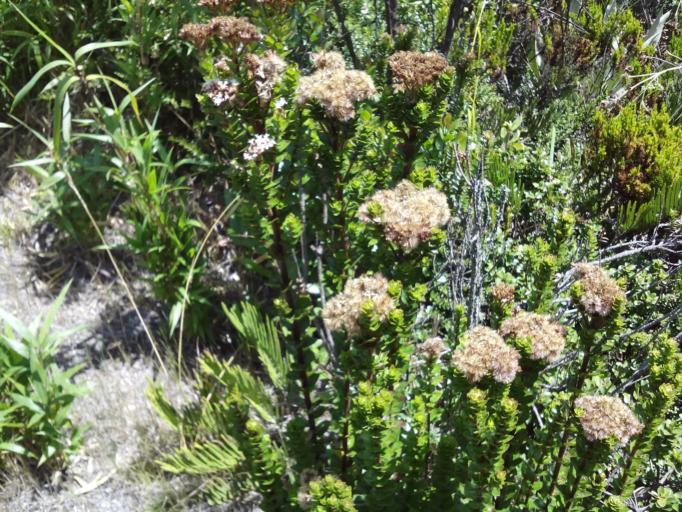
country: CO
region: Bogota D.C.
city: Bogota
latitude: 4.6054
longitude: -74.0370
